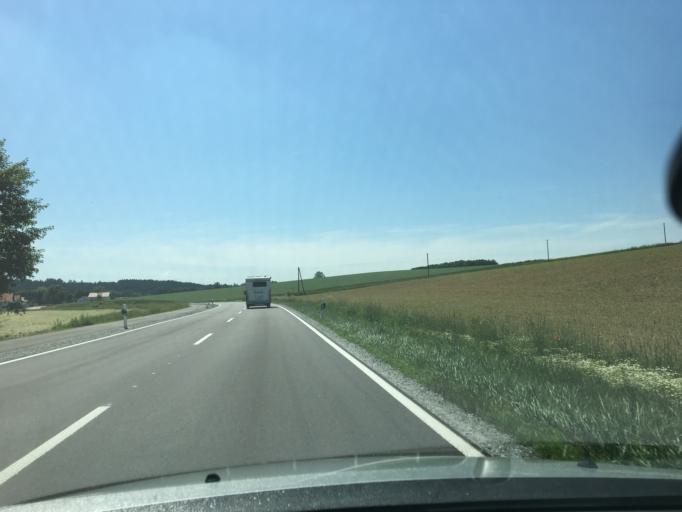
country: DE
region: Bavaria
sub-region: Upper Bavaria
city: Rohrbach
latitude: 48.3067
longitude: 12.5619
